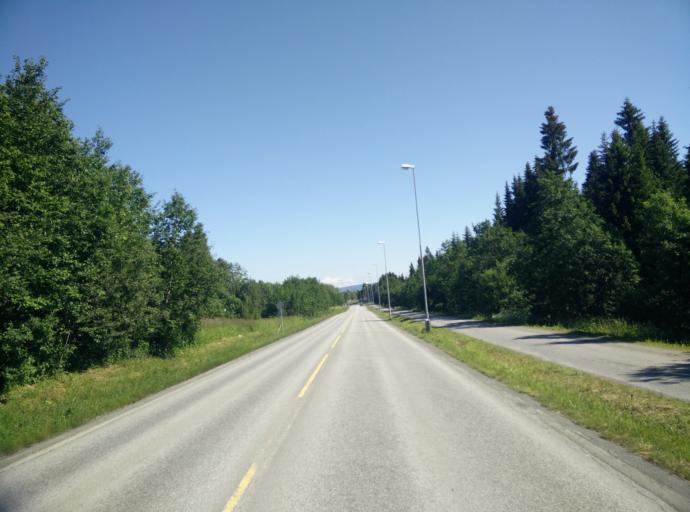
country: NO
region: Sor-Trondelag
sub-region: Trondheim
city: Trondheim
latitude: 63.3731
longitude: 10.3315
